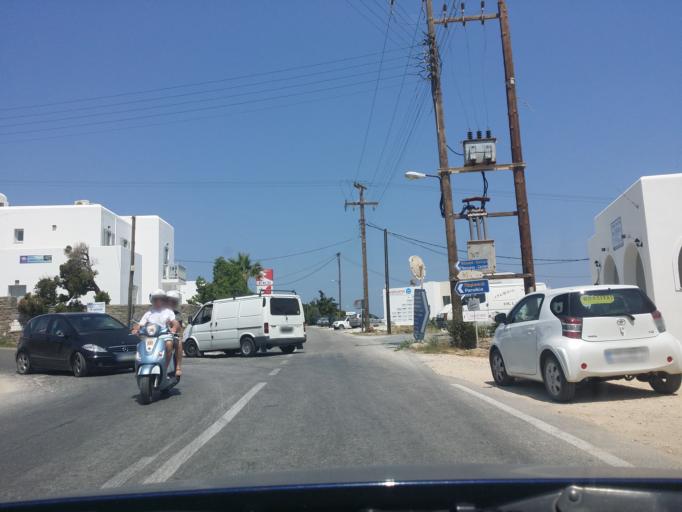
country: GR
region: South Aegean
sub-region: Nomos Kykladon
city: Naousa
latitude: 37.1179
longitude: 25.2450
